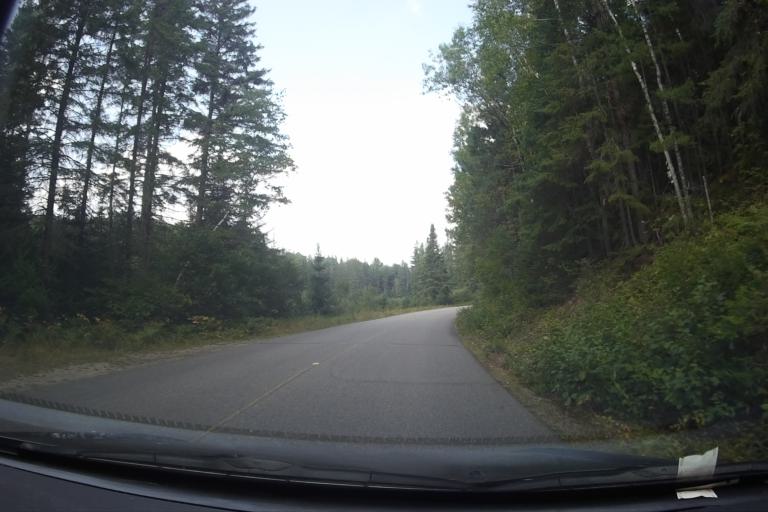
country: CA
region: Ontario
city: Bancroft
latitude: 45.6054
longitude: -78.3387
